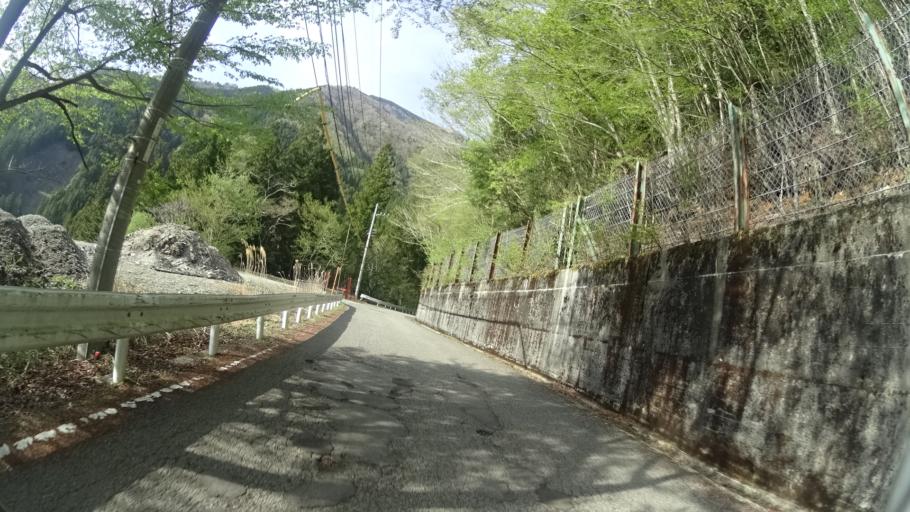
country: JP
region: Tokushima
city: Wakimachi
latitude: 33.8517
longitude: 134.0300
